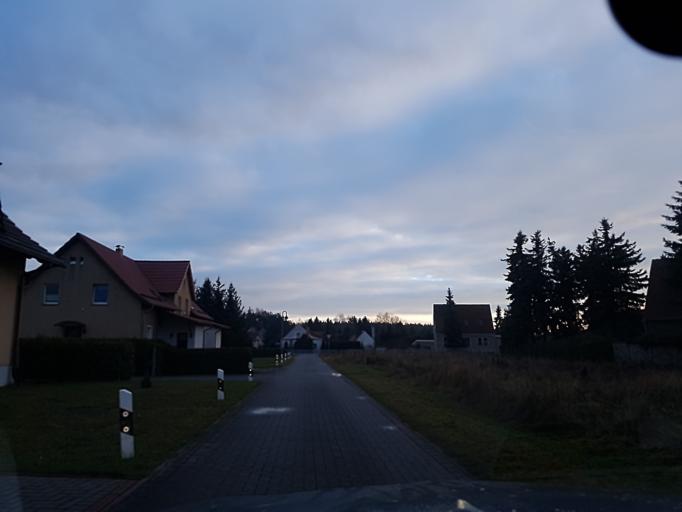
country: DE
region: Brandenburg
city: Schilda
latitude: 51.5866
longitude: 13.3873
